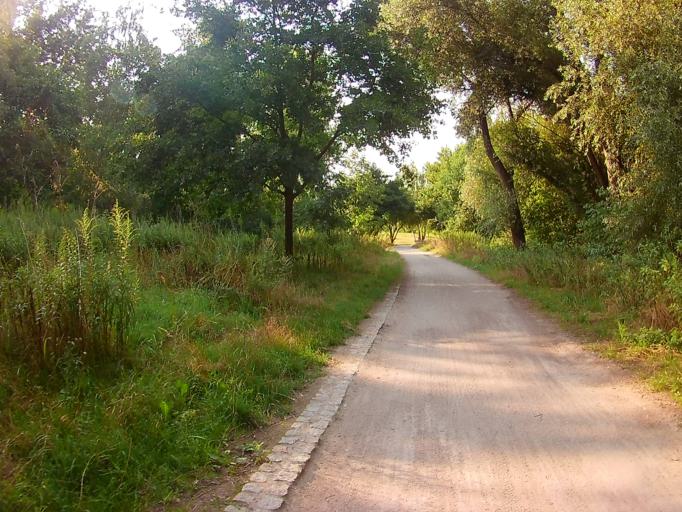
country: DE
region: Berlin
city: Kaulsdorf
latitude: 52.5099
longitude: 13.5734
